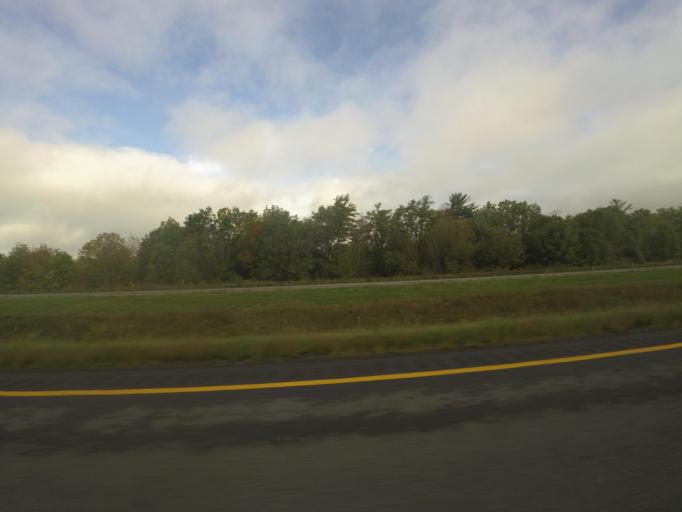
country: US
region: New York
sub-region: Delaware County
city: Sidney
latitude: 42.2961
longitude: -75.3852
